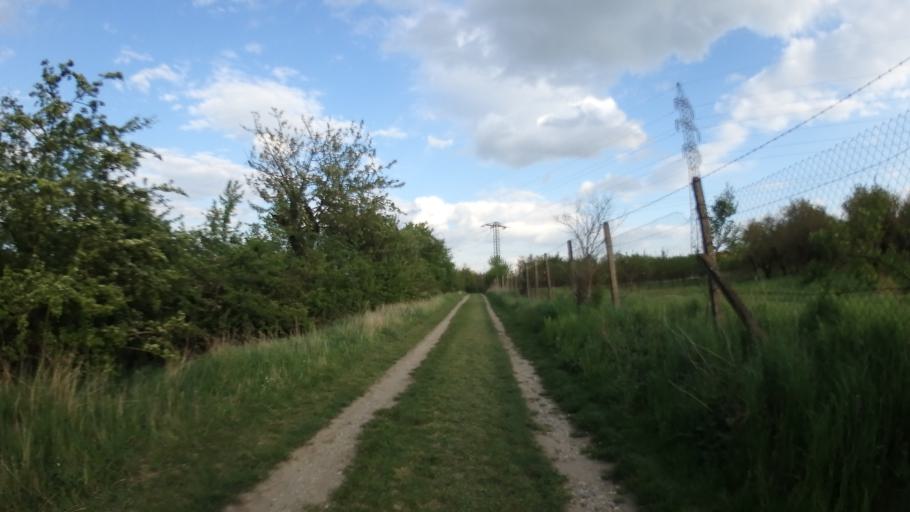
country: CZ
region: South Moravian
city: Moravany
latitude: 49.1598
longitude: 16.5732
